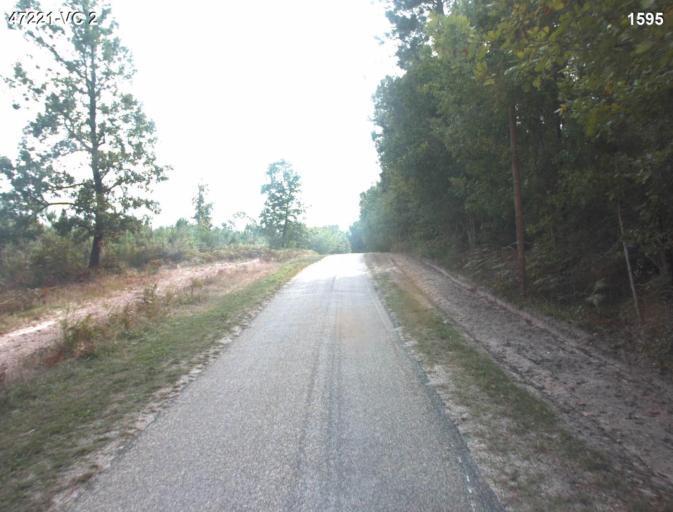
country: FR
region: Aquitaine
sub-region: Departement du Lot-et-Garonne
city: Mezin
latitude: 44.1003
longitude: 0.2277
